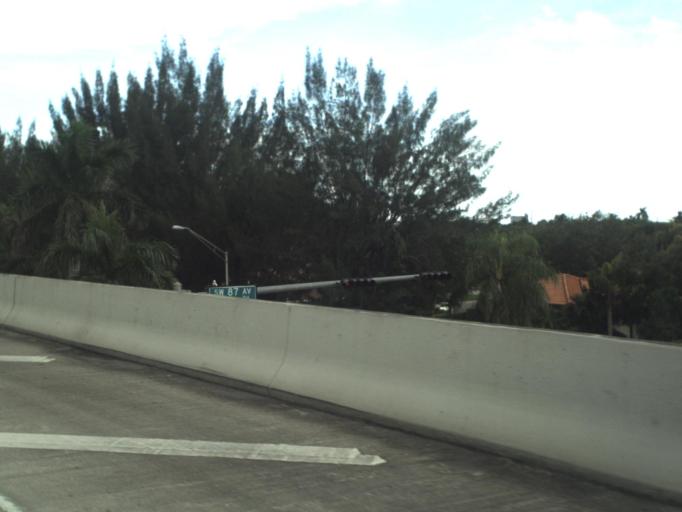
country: US
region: Florida
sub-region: Miami-Dade County
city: Glenvar Heights
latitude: 25.6956
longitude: -80.3340
